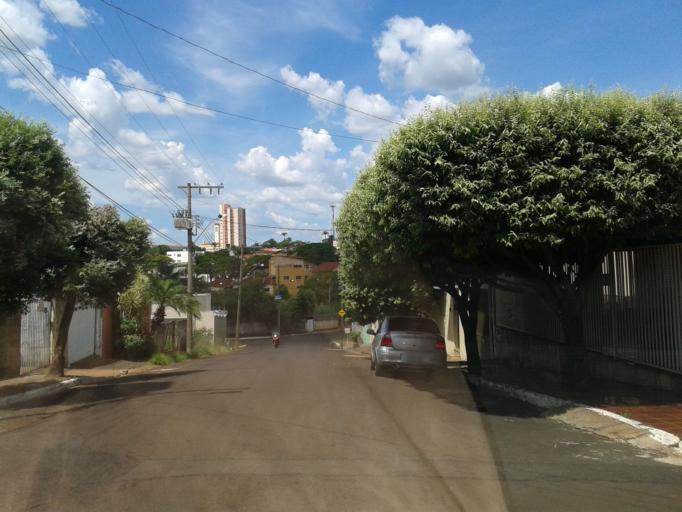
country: BR
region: Minas Gerais
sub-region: Ituiutaba
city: Ituiutaba
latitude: -18.9733
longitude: -49.4689
